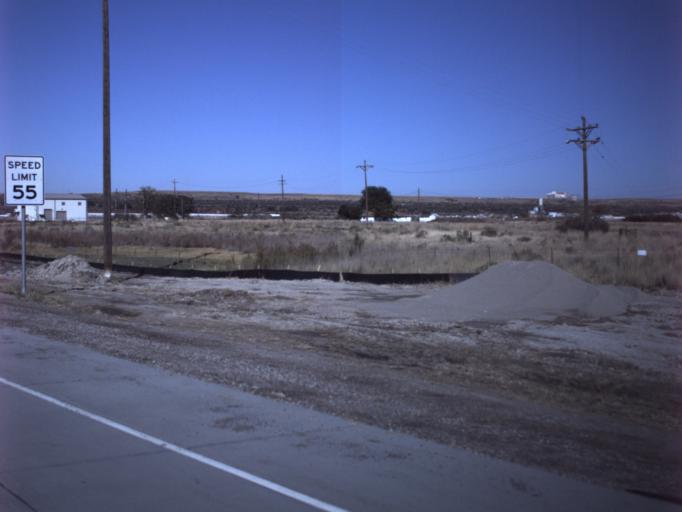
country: US
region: Utah
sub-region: Salt Lake County
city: Magna
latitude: 40.7186
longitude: -112.0672
